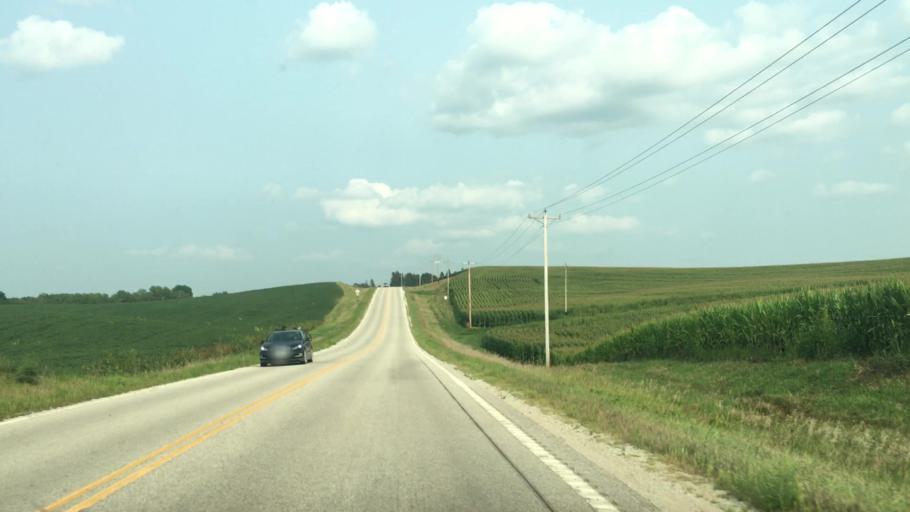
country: US
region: Minnesota
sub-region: Fillmore County
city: Preston
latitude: 43.7277
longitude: -91.9962
